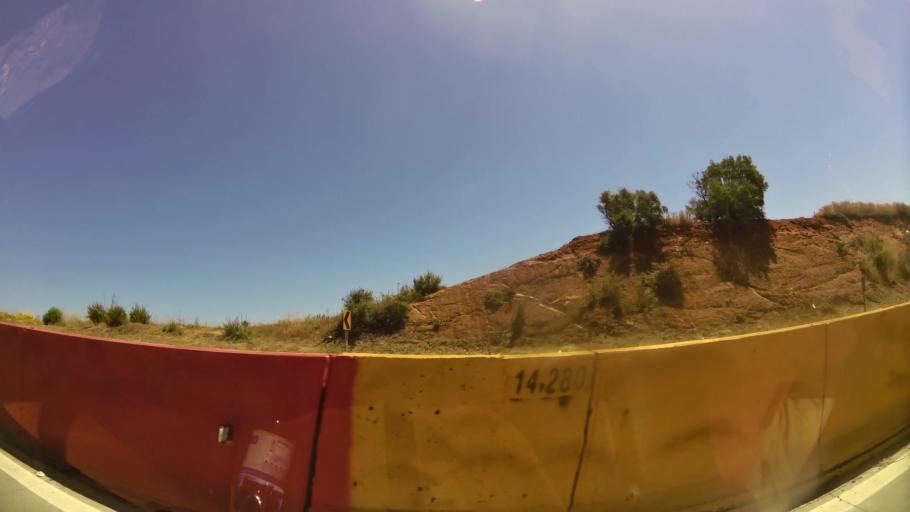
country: CL
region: Valparaiso
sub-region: Provincia de Valparaiso
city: Valparaiso
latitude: -33.0487
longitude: -71.6574
